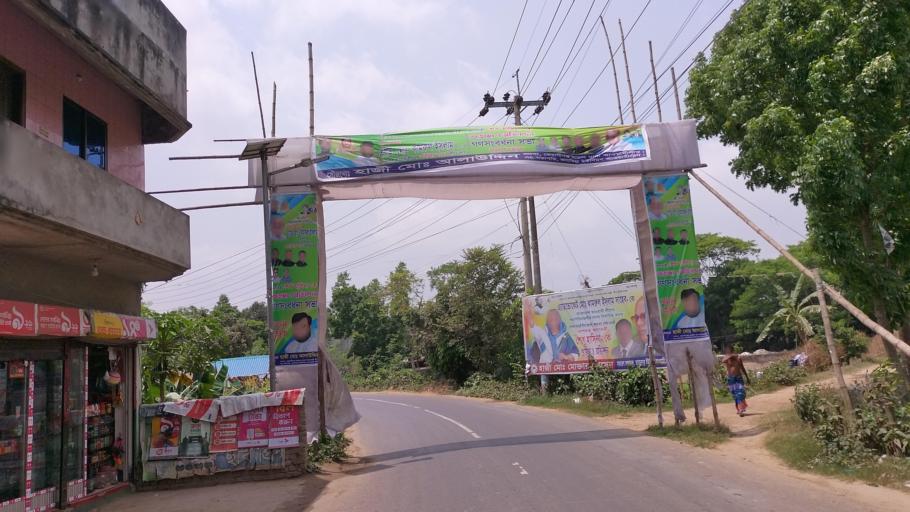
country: BD
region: Dhaka
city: Azimpur
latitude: 23.7297
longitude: 90.2968
